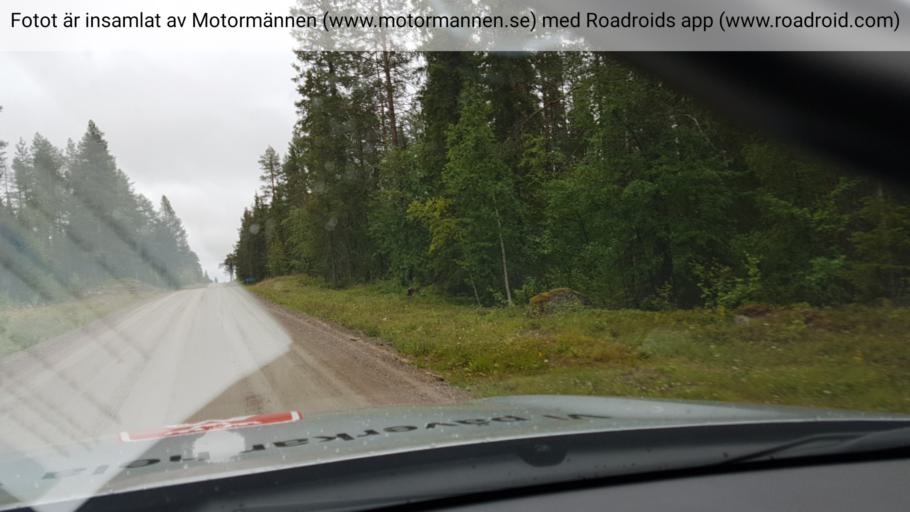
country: SE
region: Norrbotten
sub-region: Gallivare Kommun
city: Gaellivare
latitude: 66.7052
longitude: 20.4390
